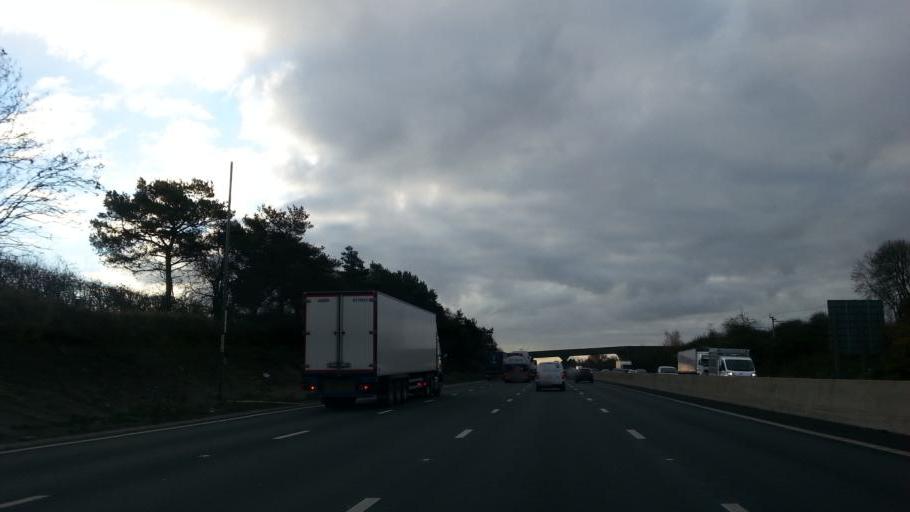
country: GB
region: England
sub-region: Northamptonshire
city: Long Buckby
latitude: 52.2982
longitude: -1.1146
